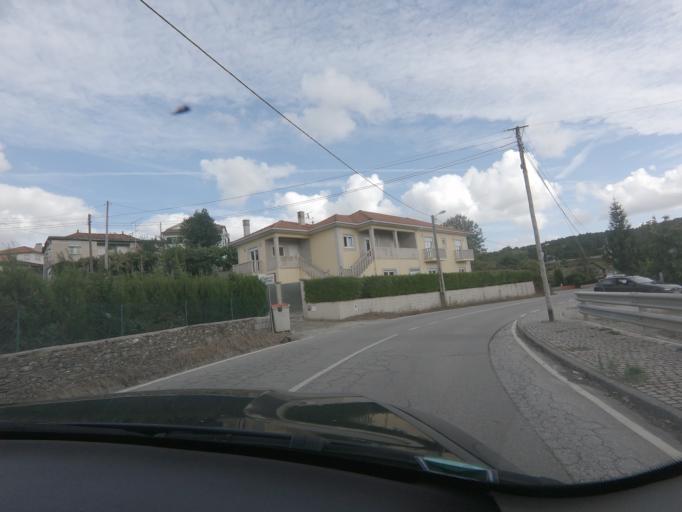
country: PT
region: Vila Real
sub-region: Vila Real
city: Vila Real
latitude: 41.2668
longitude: -7.7052
